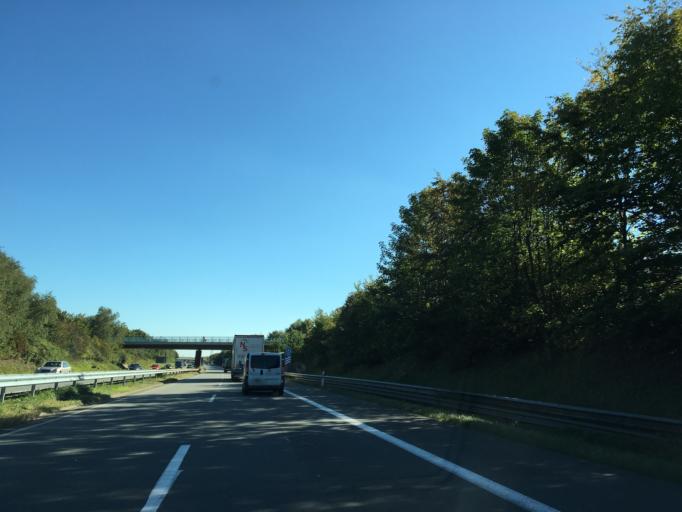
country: DE
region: Lower Saxony
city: Bardowick
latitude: 53.2819
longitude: 10.3906
